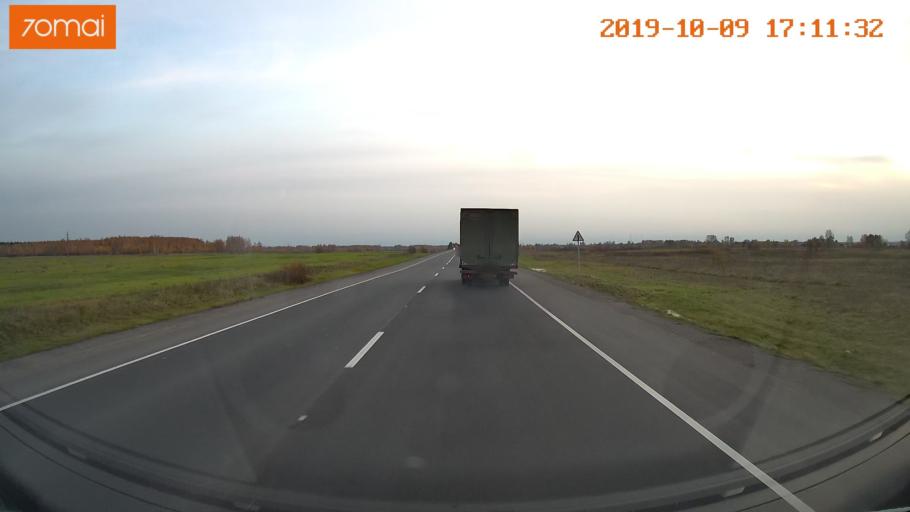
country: RU
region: Ivanovo
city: Privolzhsk
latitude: 57.3413
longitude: 41.2493
